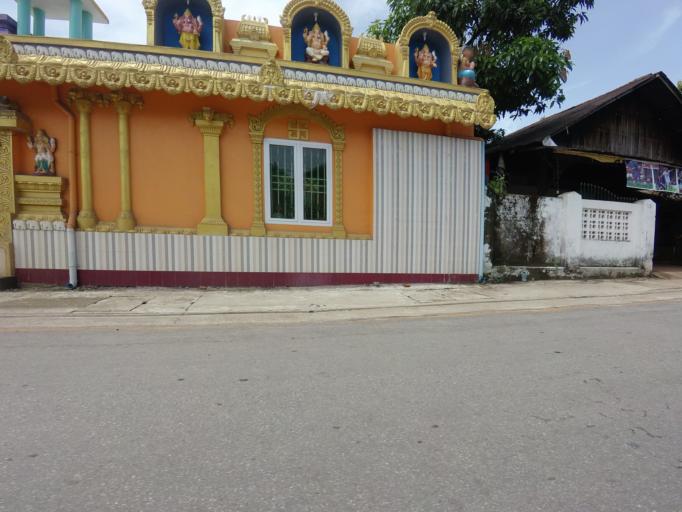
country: MM
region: Mon
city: Mawlamyine
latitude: 16.4556
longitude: 97.6330
